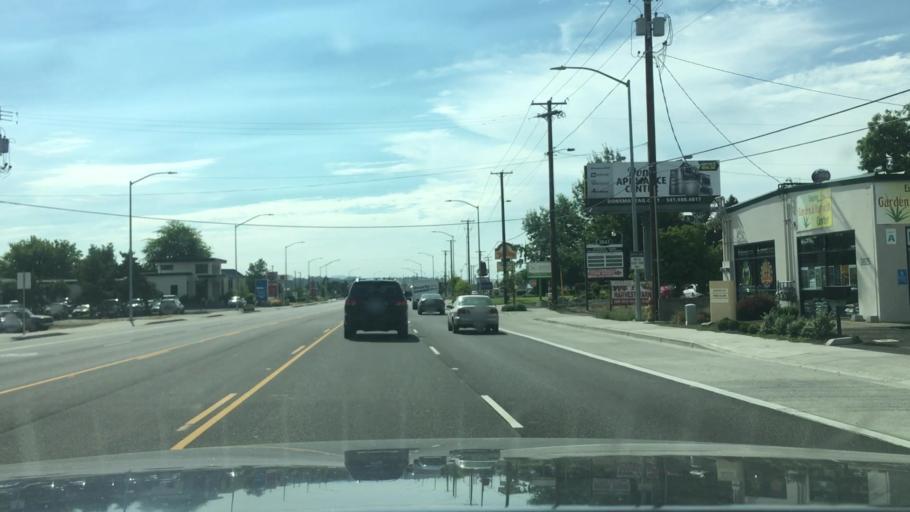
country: US
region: Oregon
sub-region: Lane County
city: Eugene
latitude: 44.0481
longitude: -123.1523
